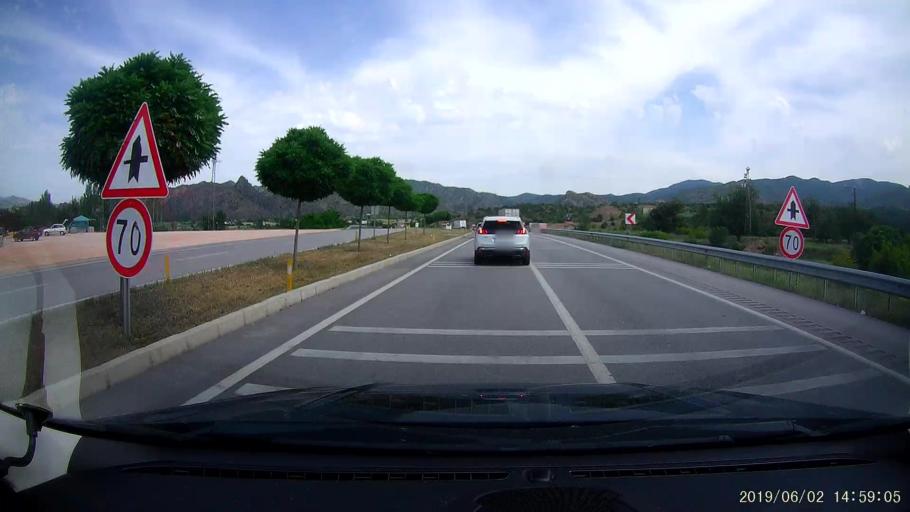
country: TR
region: Corum
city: Osmancik
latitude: 40.9727
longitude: 34.6901
